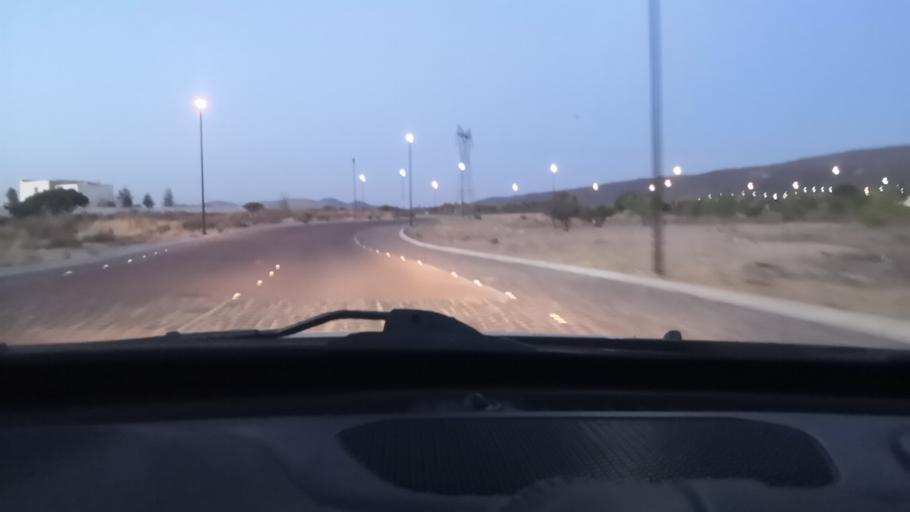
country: MX
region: Guanajuato
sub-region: Leon
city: Fraccionamiento Paseo de las Torres
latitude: 21.2320
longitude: -101.7975
